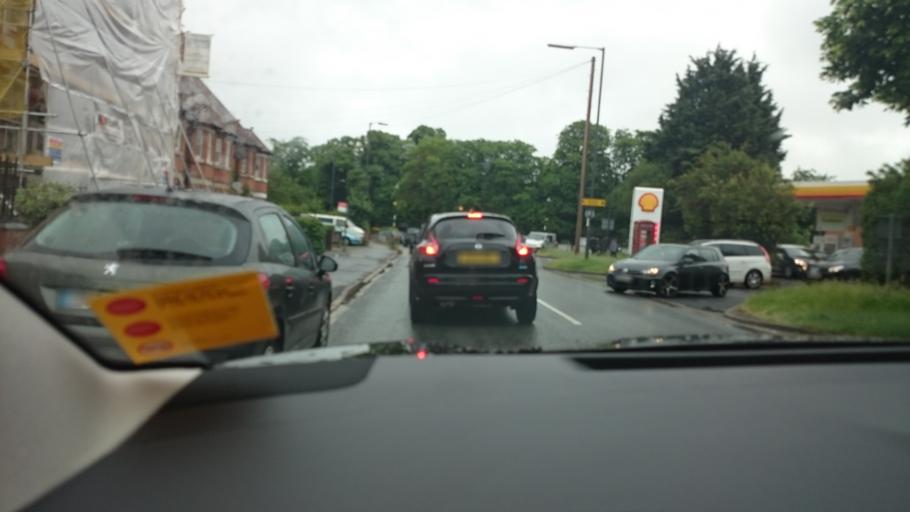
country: GB
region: England
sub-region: Warwickshire
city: Stratford-upon-Avon
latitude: 52.1896
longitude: -1.6988
